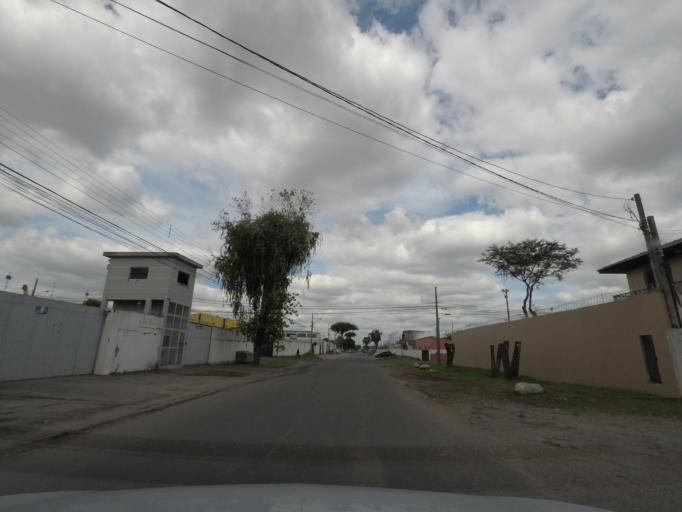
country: BR
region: Parana
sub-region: Sao Jose Dos Pinhais
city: Sao Jose dos Pinhais
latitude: -25.4880
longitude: -49.2388
